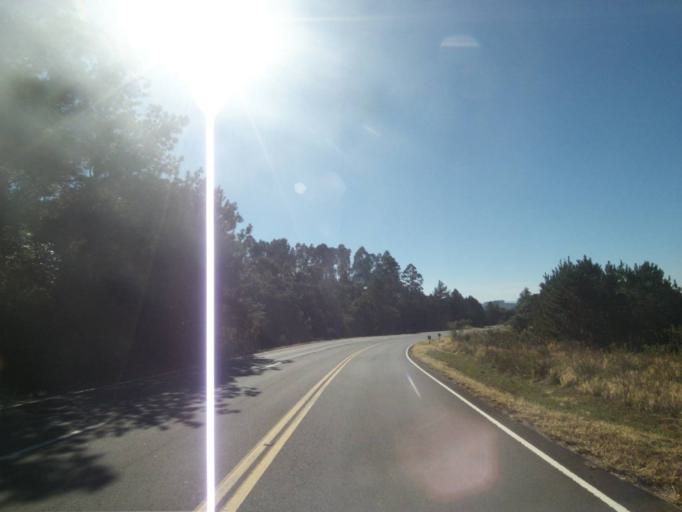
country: BR
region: Parana
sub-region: Tibagi
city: Tibagi
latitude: -24.4742
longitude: -50.5078
